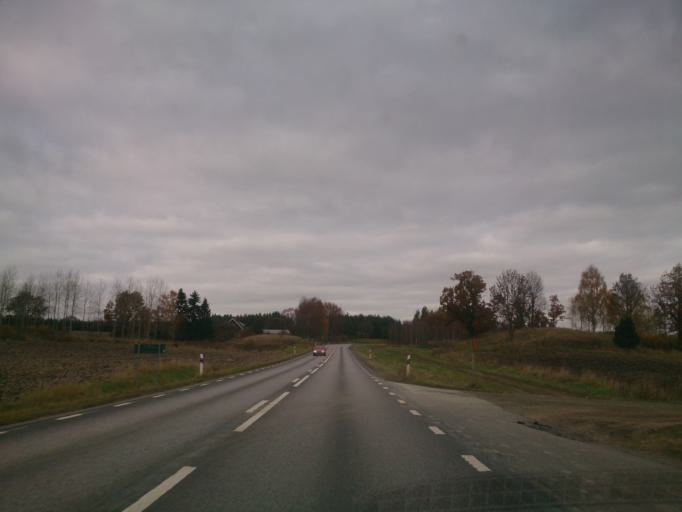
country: SE
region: OEstergoetland
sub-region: Linkopings Kommun
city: Sturefors
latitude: 58.3215
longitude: 15.8649
